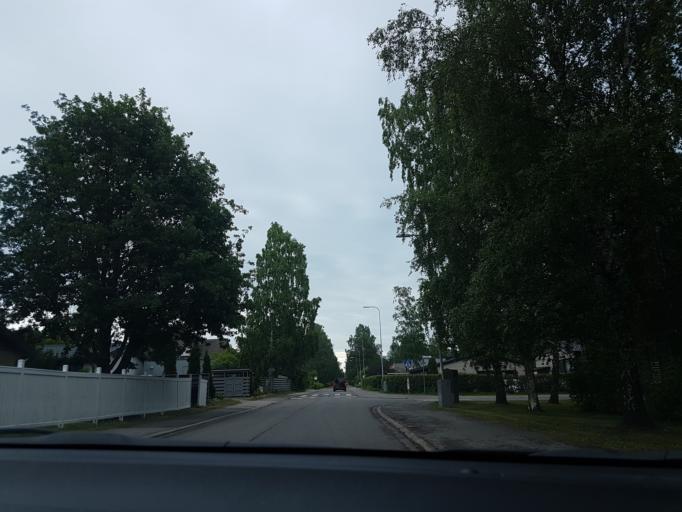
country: FI
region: Uusimaa
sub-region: Helsinki
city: Vantaa
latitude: 60.2096
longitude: 25.1273
